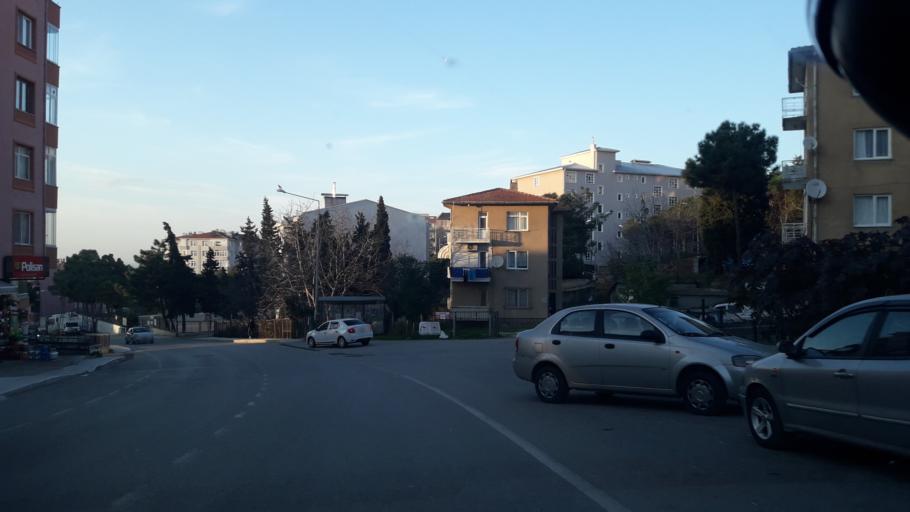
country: TR
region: Sinop
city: Sinop
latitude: 42.0269
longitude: 35.1608
